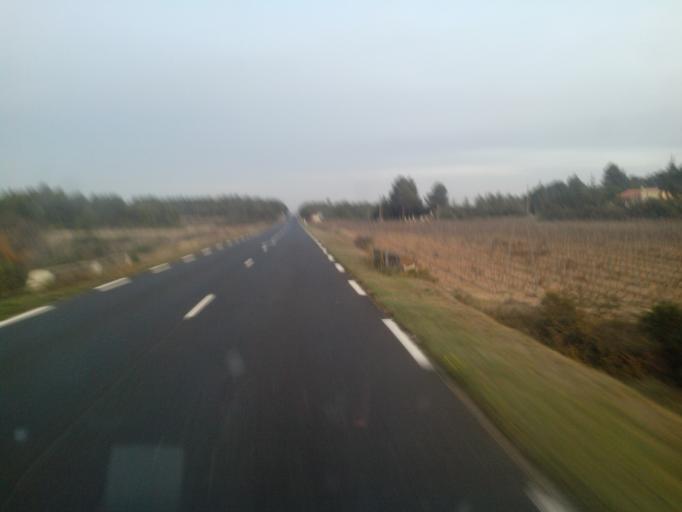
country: FR
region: Languedoc-Roussillon
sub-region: Departement de l'Herault
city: Olonzac
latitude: 43.2762
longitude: 2.7970
